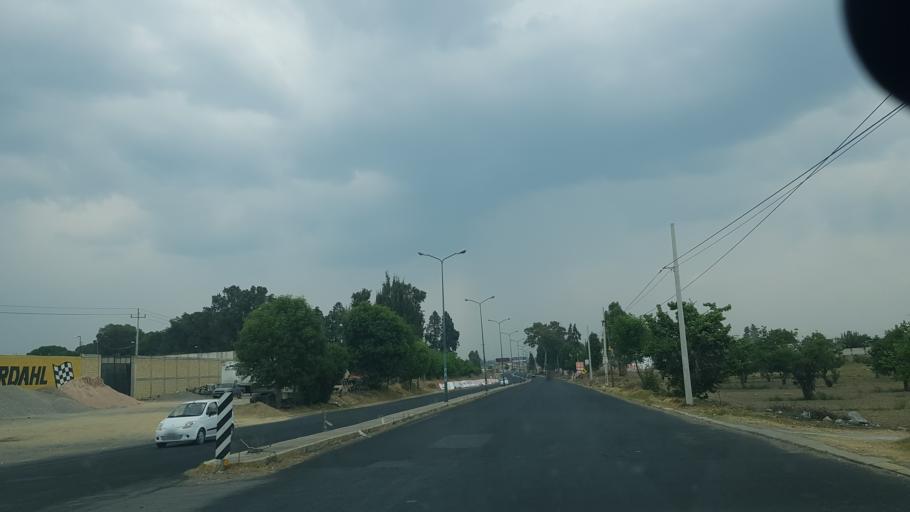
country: MX
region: Puebla
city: Huejotzingo
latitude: 19.1737
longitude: -98.4136
